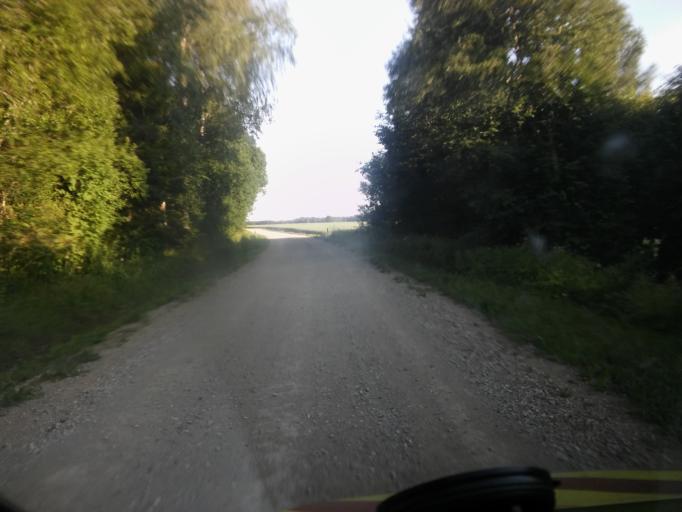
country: EE
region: Valgamaa
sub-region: Torva linn
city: Torva
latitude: 58.0719
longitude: 25.9022
